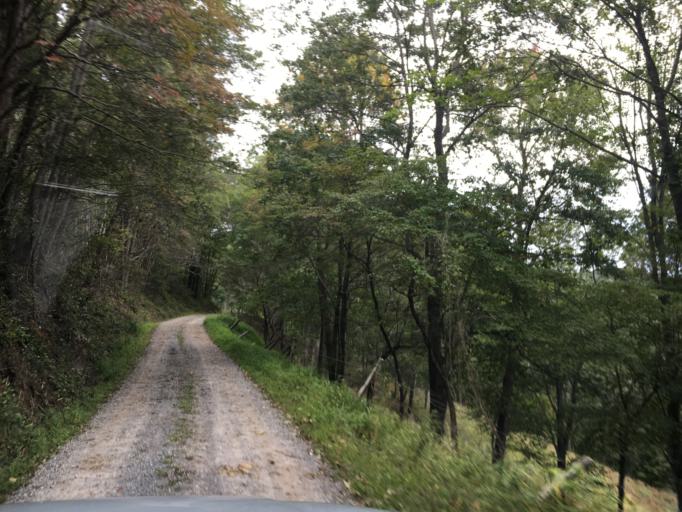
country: US
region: North Carolina
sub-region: Haywood County
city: Clyde
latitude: 35.5543
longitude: -82.9140
